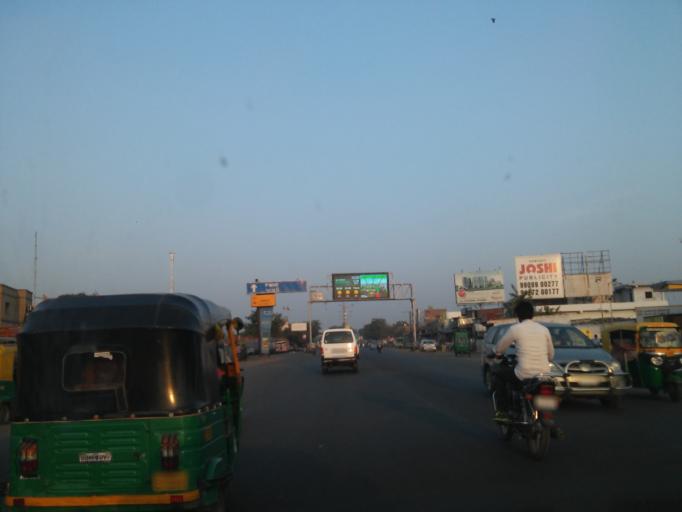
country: IN
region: Gujarat
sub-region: Ahmadabad
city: Sarkhej
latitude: 22.9960
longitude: 72.5358
